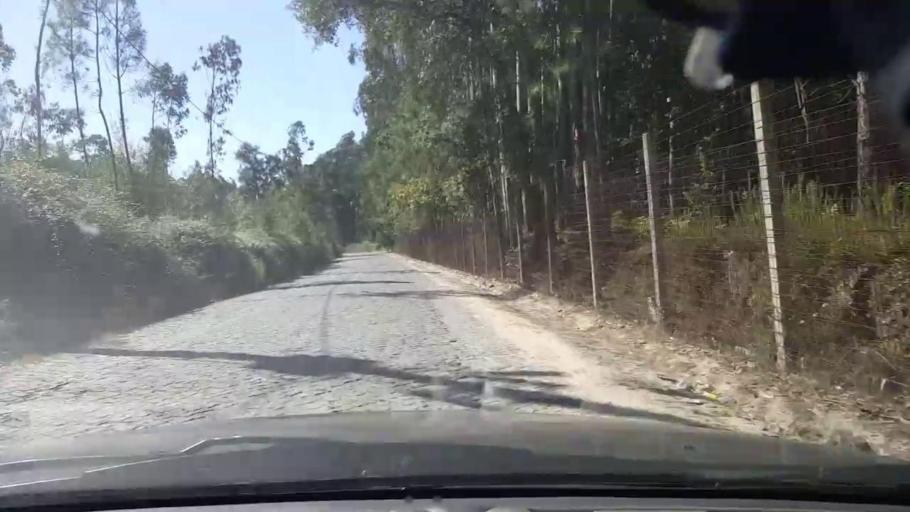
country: PT
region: Porto
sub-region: Maia
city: Gemunde
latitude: 41.2965
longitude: -8.6654
